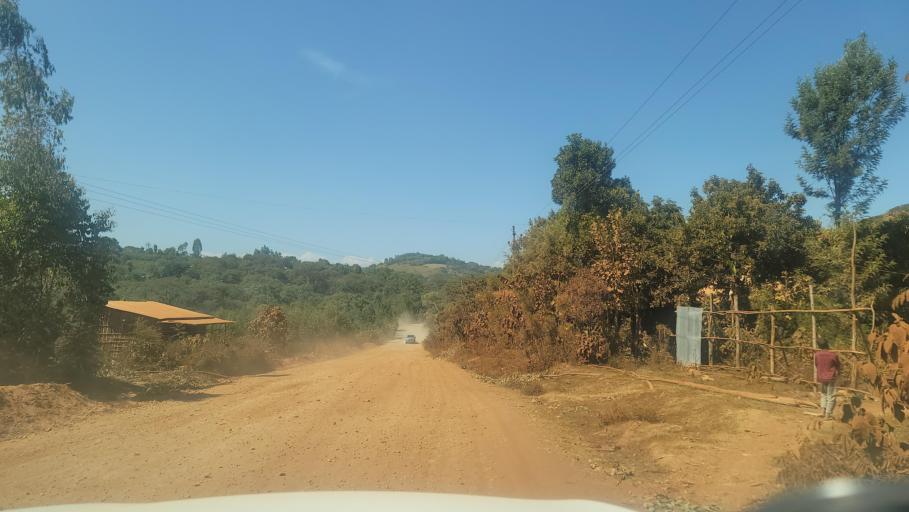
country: ET
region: Oromiya
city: Agaro
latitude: 7.8340
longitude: 36.5431
